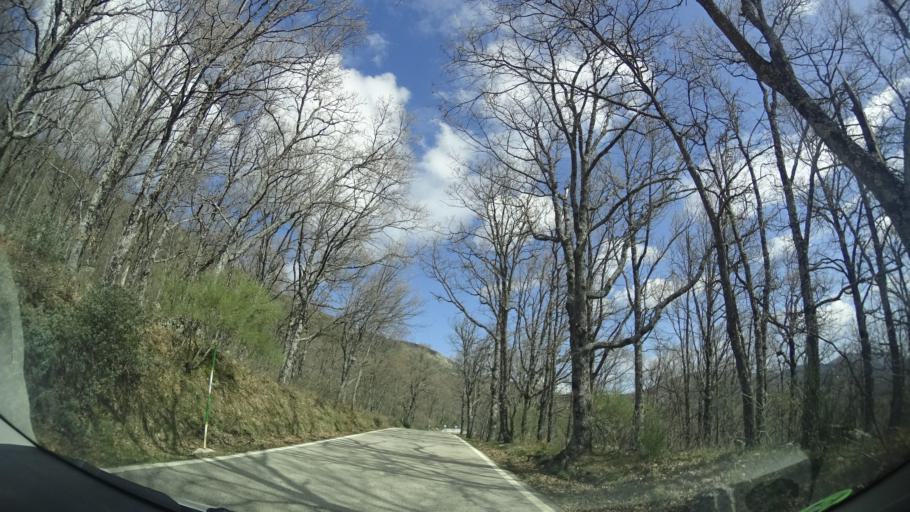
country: ES
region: Madrid
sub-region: Provincia de Madrid
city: Miraflores de la Sierra
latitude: 40.8344
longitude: -3.7699
